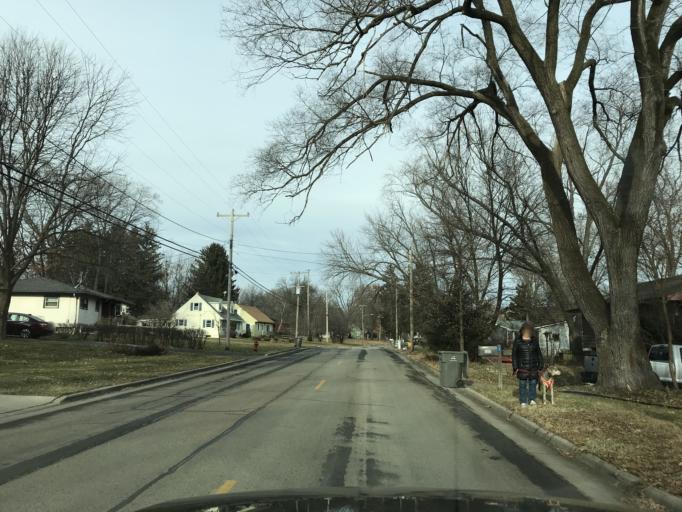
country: US
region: Wisconsin
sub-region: Dane County
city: Monona
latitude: 43.0616
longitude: -89.3458
